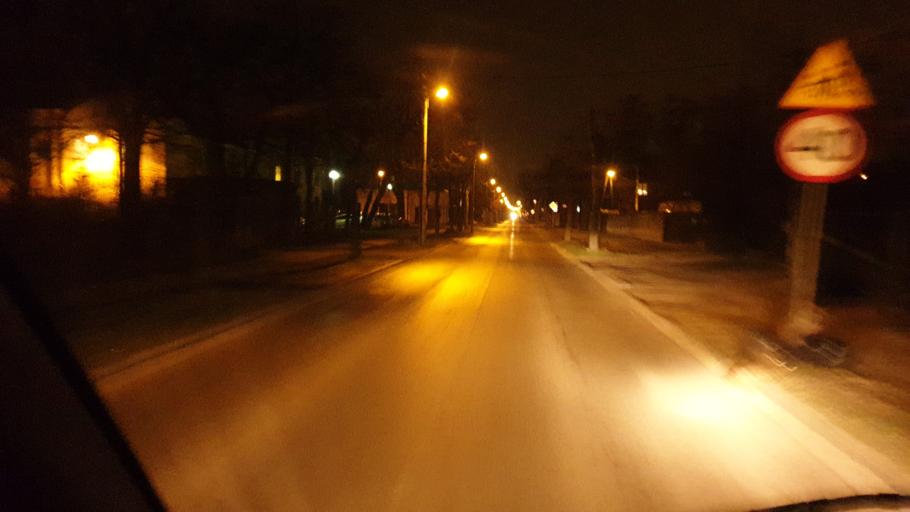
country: PL
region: Lodz Voivodeship
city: Lodz
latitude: 51.7163
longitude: 19.4495
